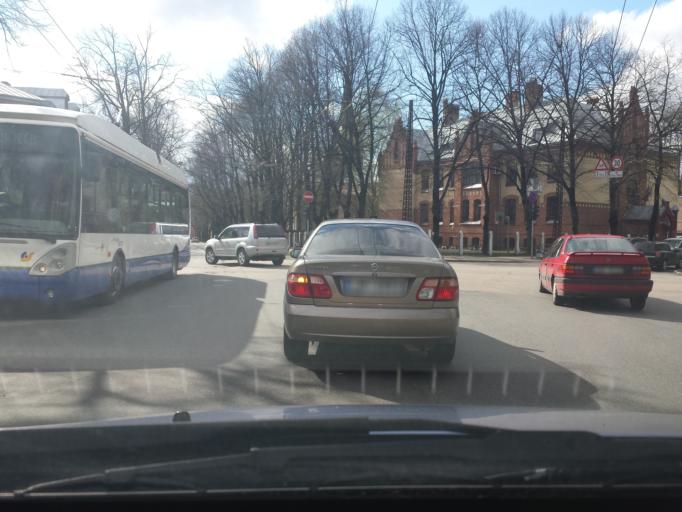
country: LV
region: Riga
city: Riga
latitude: 56.9537
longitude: 24.1523
